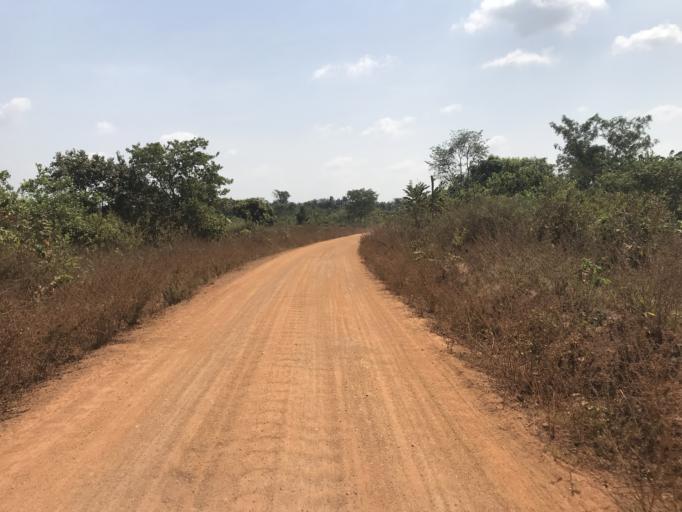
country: NG
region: Osun
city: Ifon
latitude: 7.9220
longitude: 4.4823
